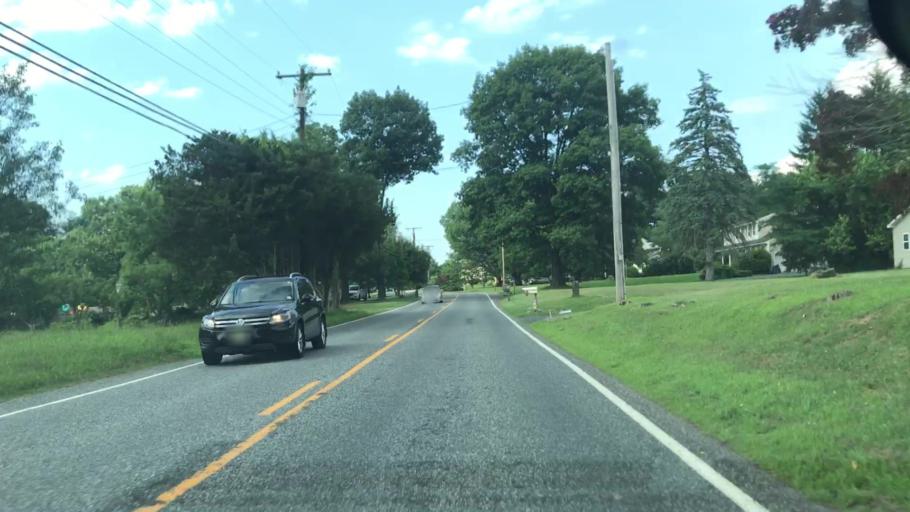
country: US
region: New Jersey
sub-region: Hunterdon County
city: Flemington
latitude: 40.4973
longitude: -74.8082
